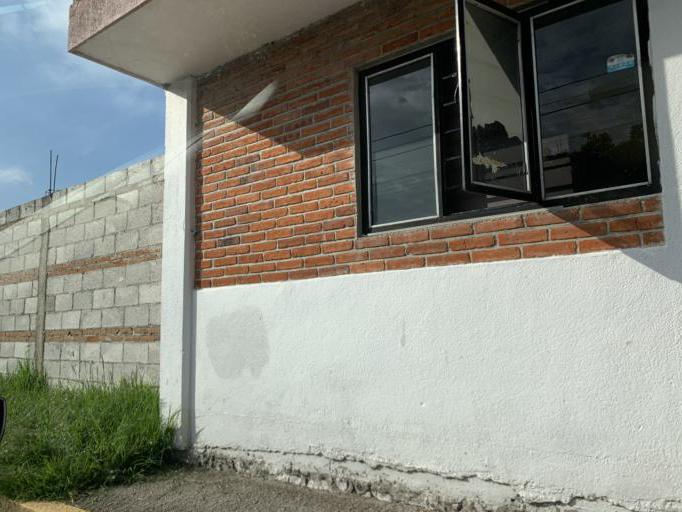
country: MX
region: Puebla
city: San Andres Cholula
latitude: 19.0522
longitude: -98.2929
